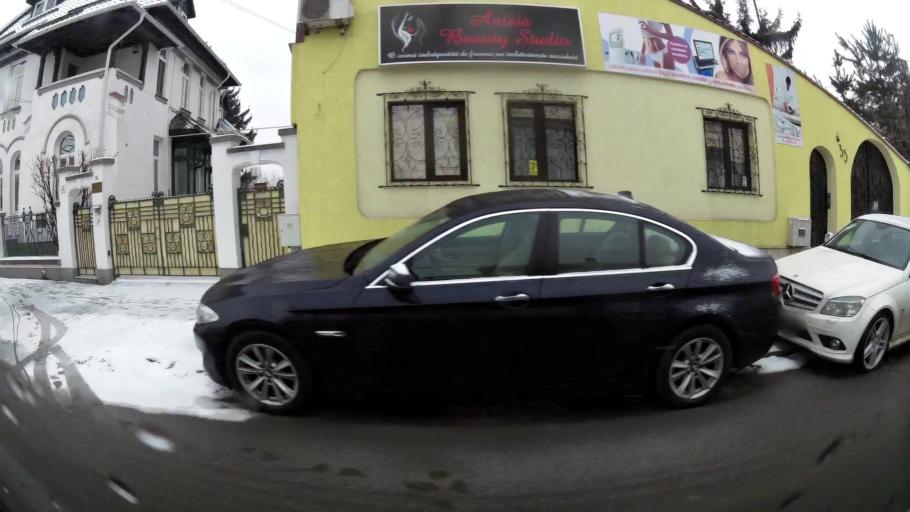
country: RO
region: Prahova
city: Ploiesti
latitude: 44.9349
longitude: 26.0208
